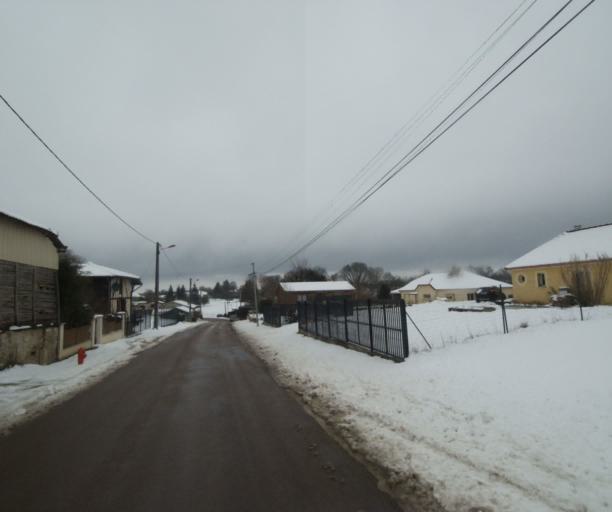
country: FR
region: Champagne-Ardenne
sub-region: Departement de la Haute-Marne
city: Laneuville-a-Remy
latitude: 48.5013
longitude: 4.8693
